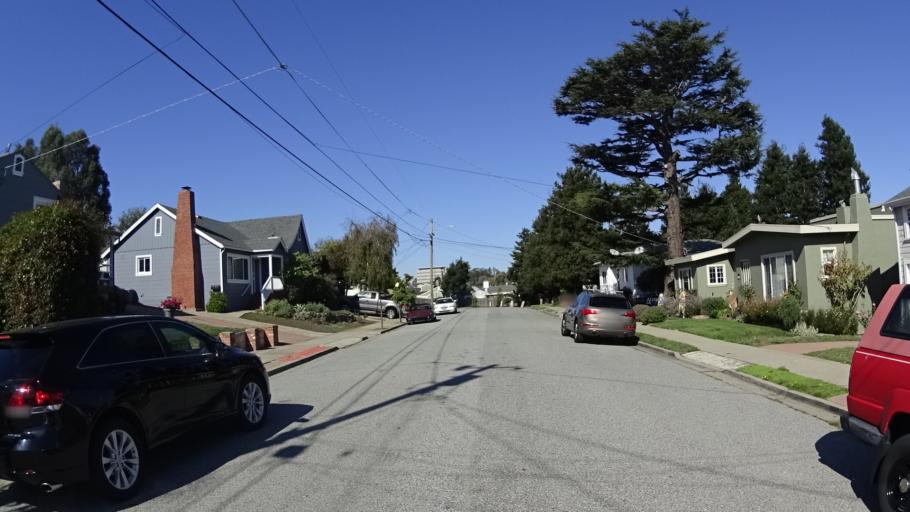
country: US
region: California
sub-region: San Mateo County
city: San Bruno
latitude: 37.6217
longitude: -122.4197
